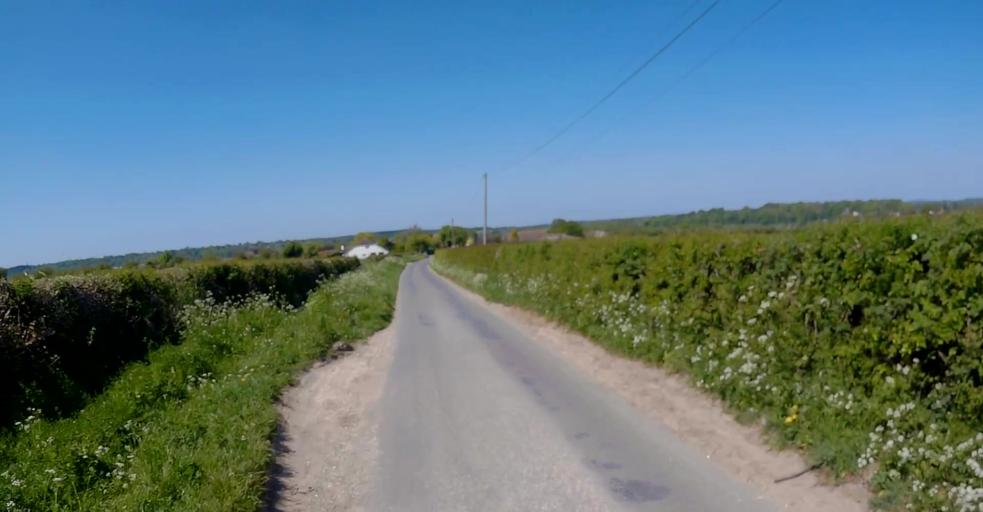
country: GB
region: England
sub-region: Hampshire
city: Overton
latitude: 51.2209
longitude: -1.3252
